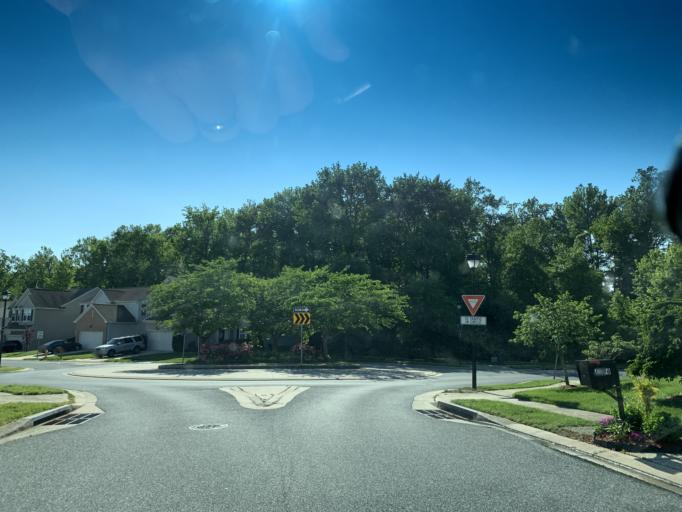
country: US
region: Maryland
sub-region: Harford County
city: Riverside
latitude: 39.4840
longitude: -76.2379
